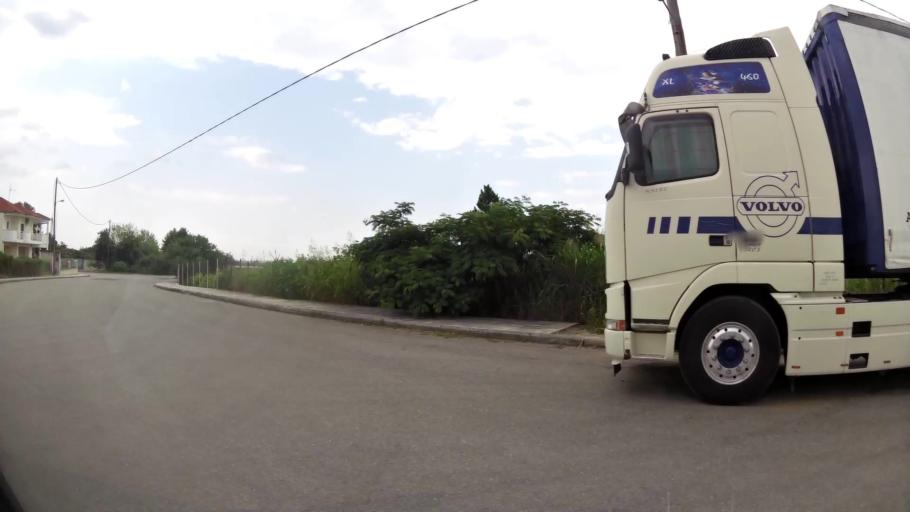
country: GR
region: Central Macedonia
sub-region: Nomos Imathias
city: Veroia
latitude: 40.5311
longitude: 22.2097
